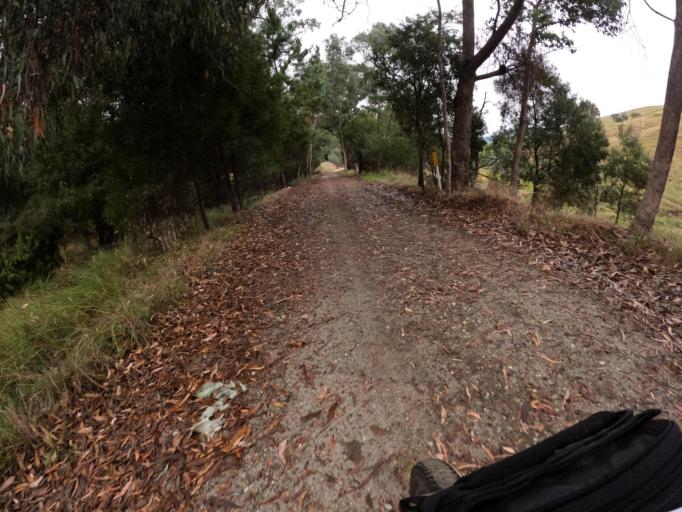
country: AU
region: New South Wales
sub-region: Greater Hume Shire
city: Holbrook
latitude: -36.1583
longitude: 147.4104
